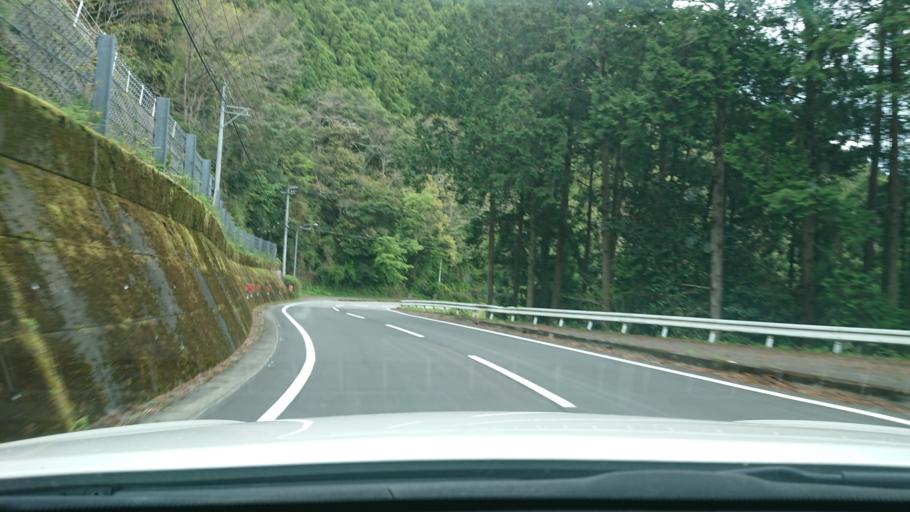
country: JP
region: Tokushima
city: Ishii
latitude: 33.9072
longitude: 134.4204
